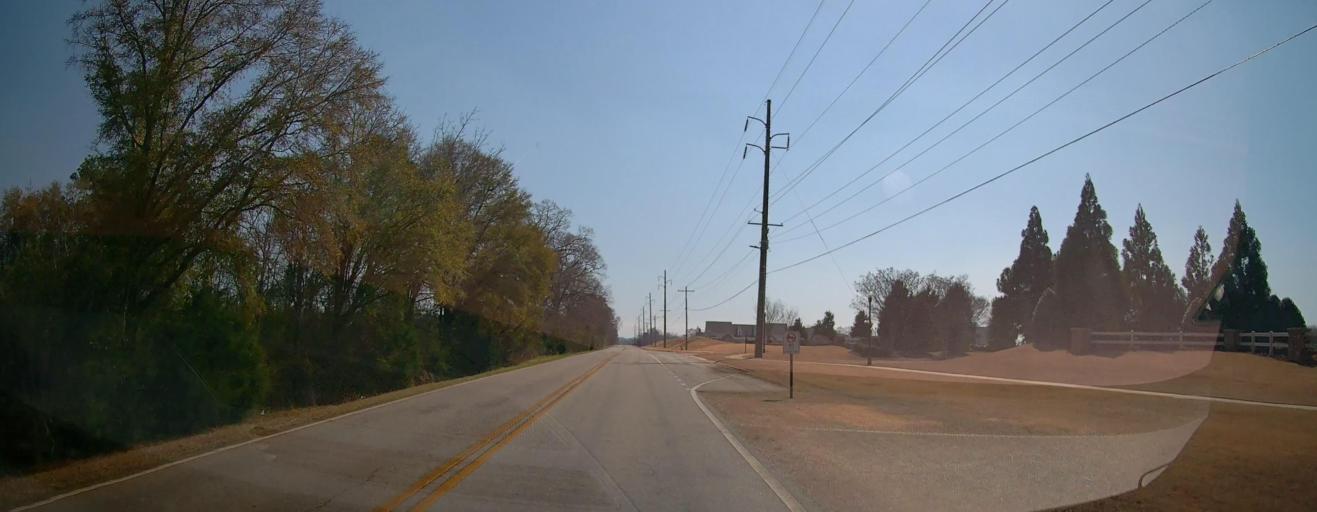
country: US
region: Georgia
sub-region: Houston County
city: Perry
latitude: 32.4776
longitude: -83.7590
